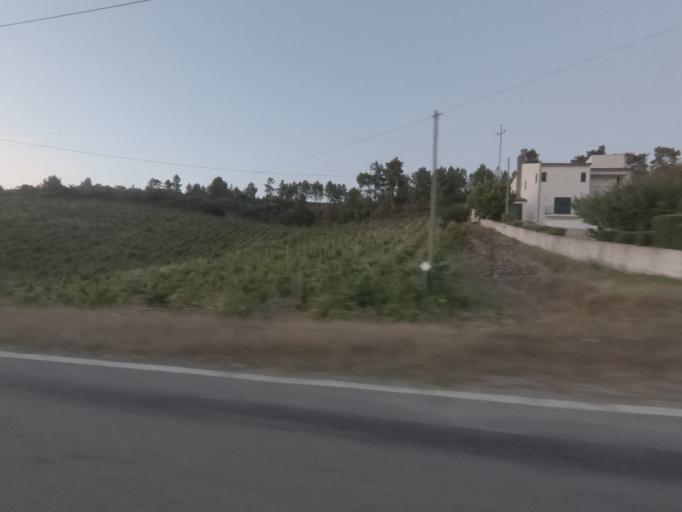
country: PT
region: Viseu
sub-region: Armamar
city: Armamar
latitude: 41.2011
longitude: -7.6982
